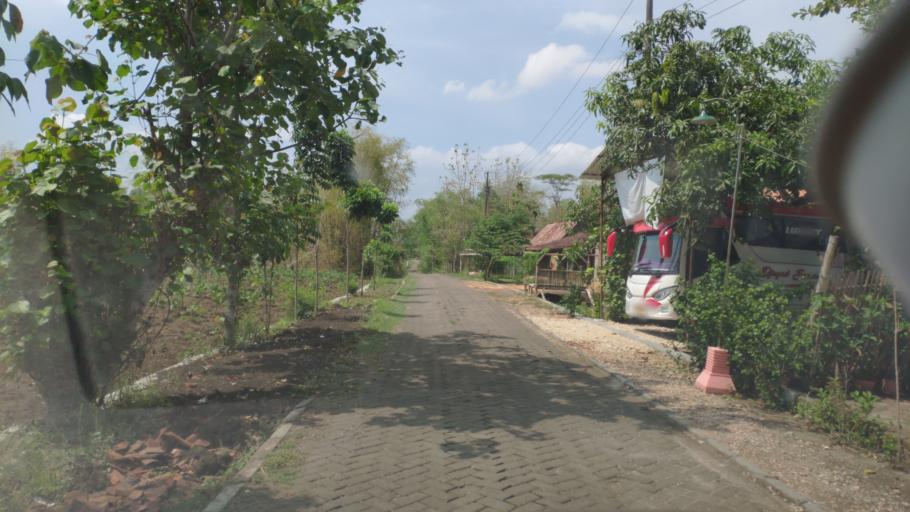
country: ID
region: Central Java
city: Balongrejo
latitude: -7.0143
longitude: 111.3694
